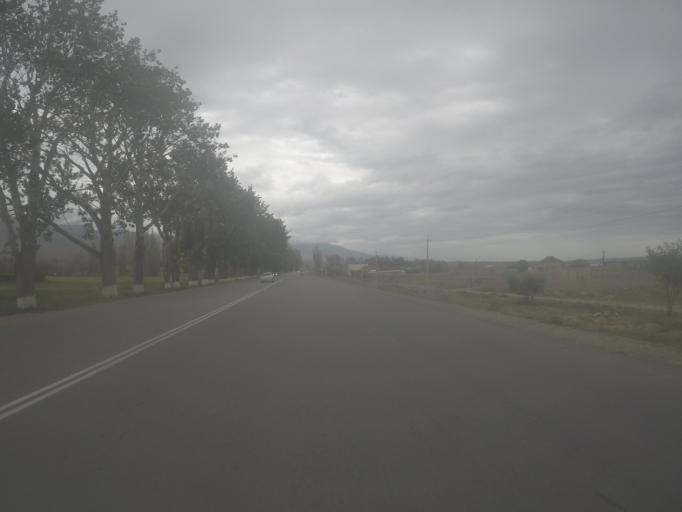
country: KG
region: Ysyk-Koel
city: Cholpon-Ata
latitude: 42.5905
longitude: 76.7514
